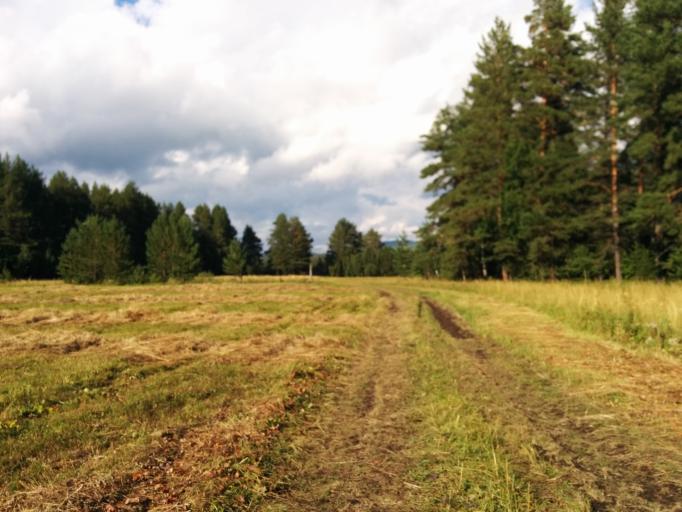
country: RU
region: Bashkortostan
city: Beloretsk
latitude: 54.0444
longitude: 58.3230
